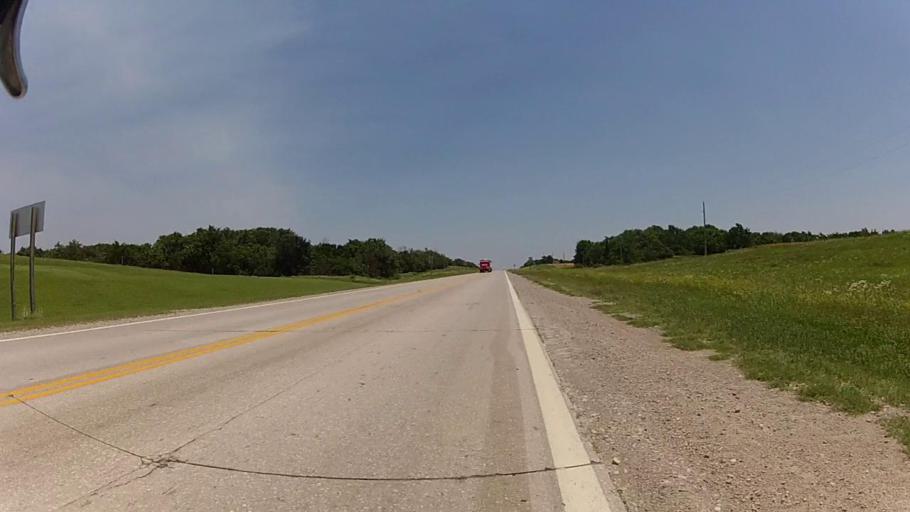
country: US
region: Kansas
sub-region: Sumner County
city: Caldwell
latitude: 37.0566
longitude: -97.3984
